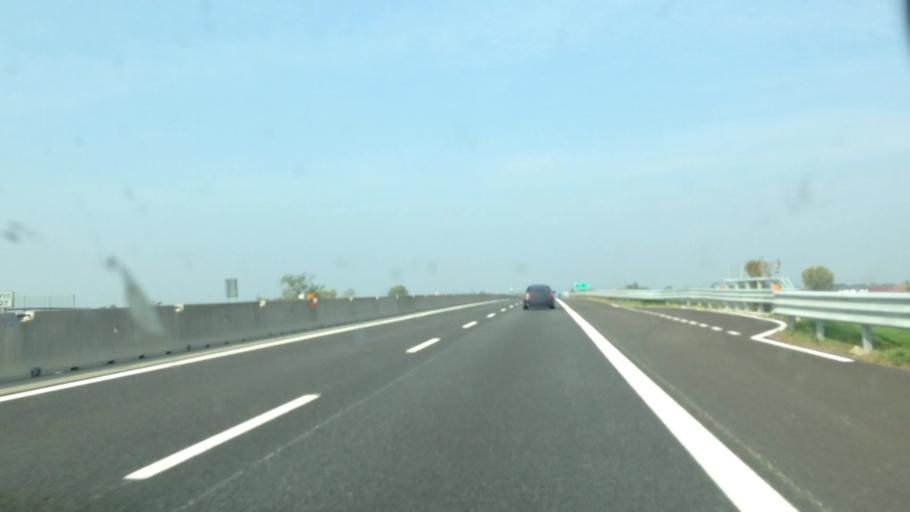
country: IT
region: Piedmont
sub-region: Provincia di Vercelli
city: Santhia
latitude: 45.3599
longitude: 8.1600
